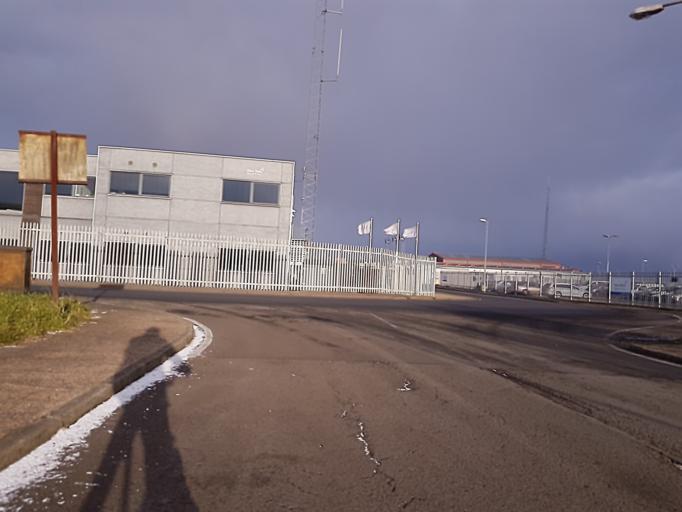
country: GB
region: England
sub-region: North East Lincolnshire
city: Grimsby
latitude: 53.5780
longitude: -0.0569
